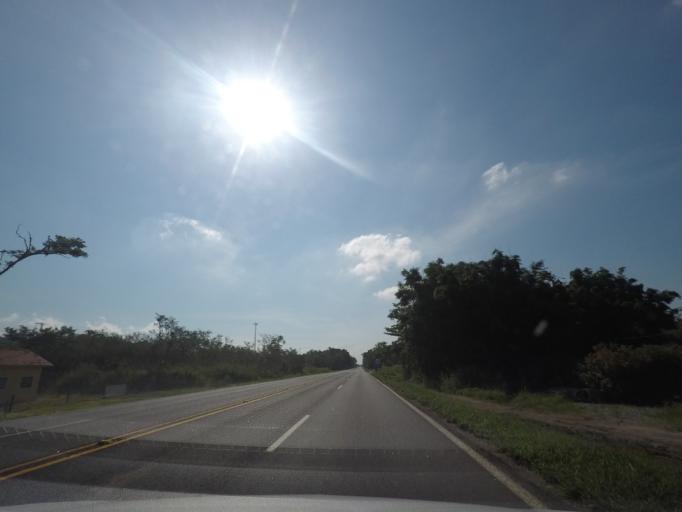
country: BR
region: Parana
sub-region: Pontal Do Parana
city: Pontal do Parana
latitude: -25.6461
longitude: -48.5895
